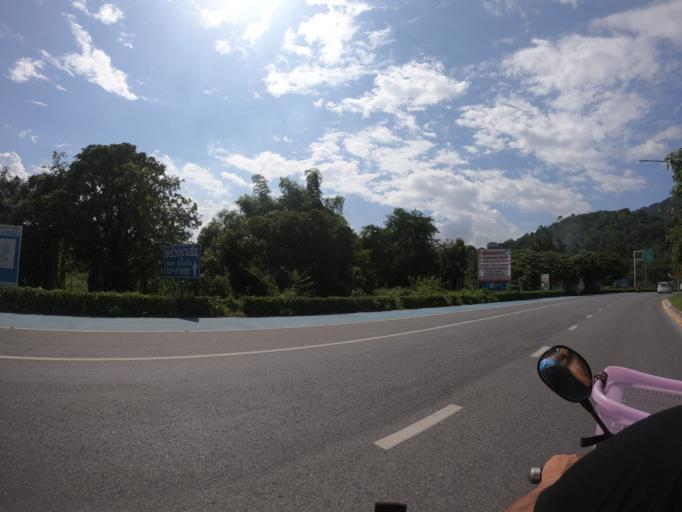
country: TH
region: Nakhon Nayok
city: Nakhon Nayok
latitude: 14.3203
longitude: 101.3113
